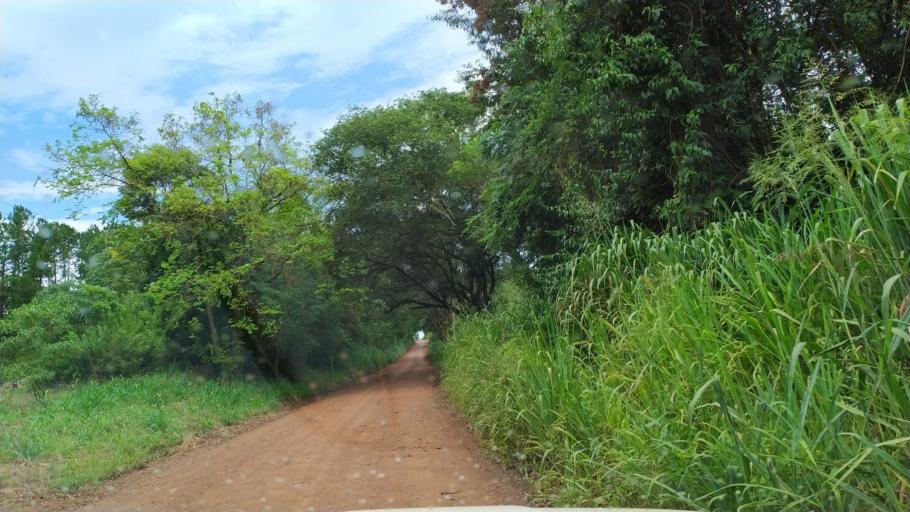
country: AR
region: Misiones
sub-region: Departamento de Eldorado
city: Eldorado
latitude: -26.4318
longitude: -54.6046
